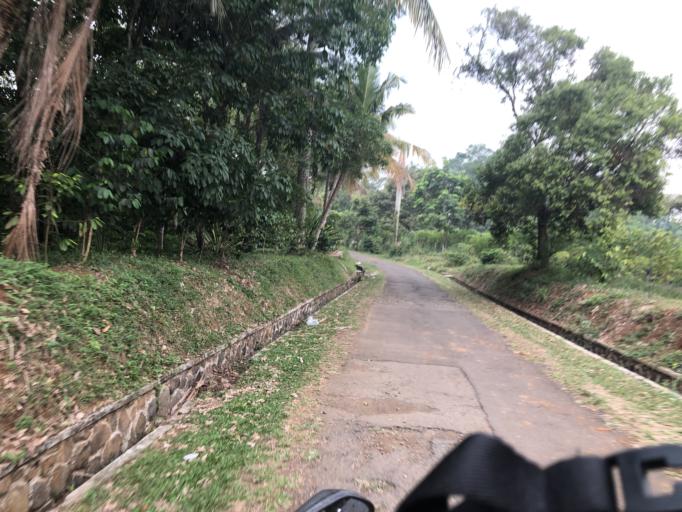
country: ID
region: West Java
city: Ciampea
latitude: -6.5523
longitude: 106.7172
